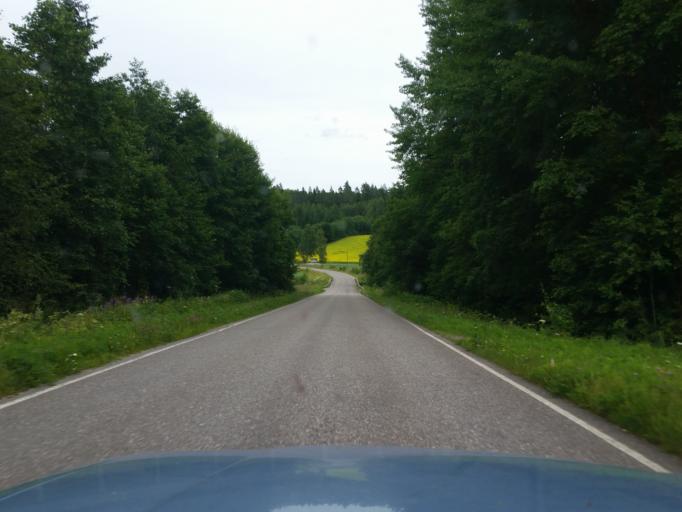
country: FI
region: Uusimaa
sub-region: Helsinki
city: Sammatti
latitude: 60.4362
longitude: 23.8375
